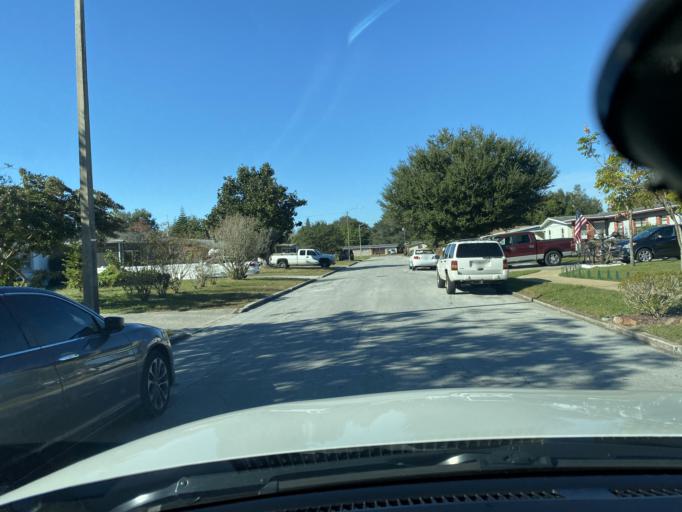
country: US
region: Florida
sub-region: Orange County
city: Azalea Park
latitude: 28.5293
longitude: -81.3156
